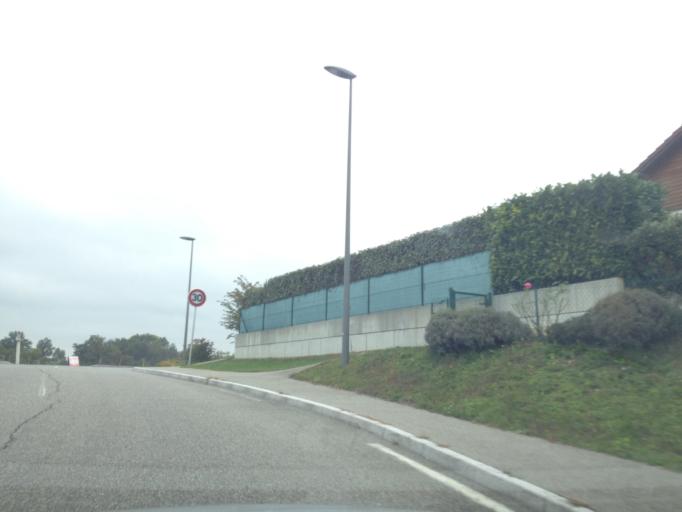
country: FR
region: Rhone-Alpes
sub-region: Departement de la Haute-Savoie
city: Seynod
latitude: 45.8763
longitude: 6.0841
